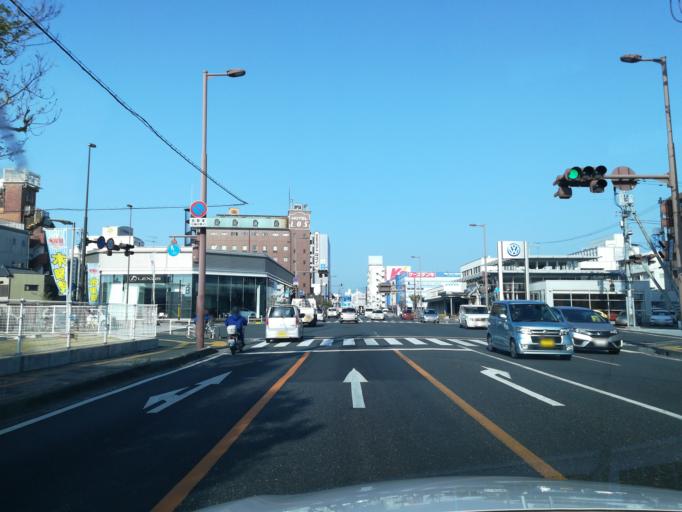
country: JP
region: Kochi
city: Kochi-shi
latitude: 33.5659
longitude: 133.5486
